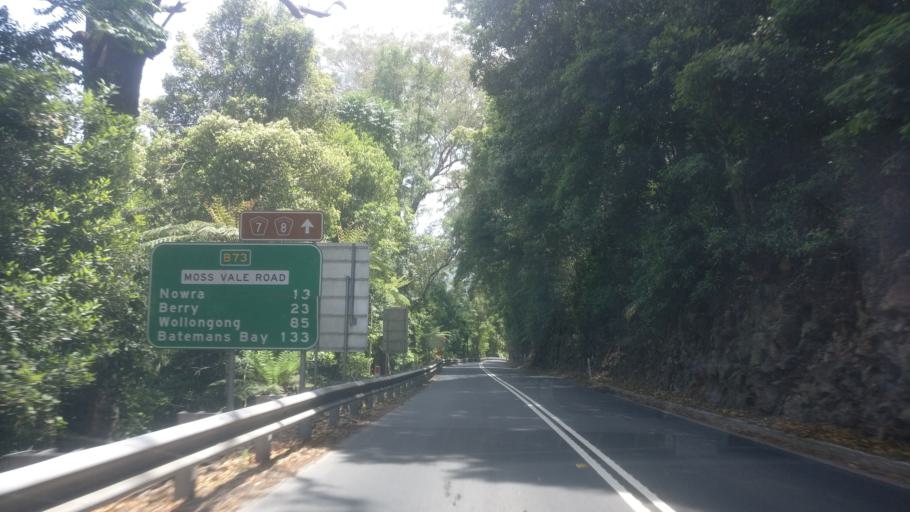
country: AU
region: New South Wales
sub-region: Shoalhaven Shire
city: Kangaroo Valley
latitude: -34.7898
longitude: 150.5650
